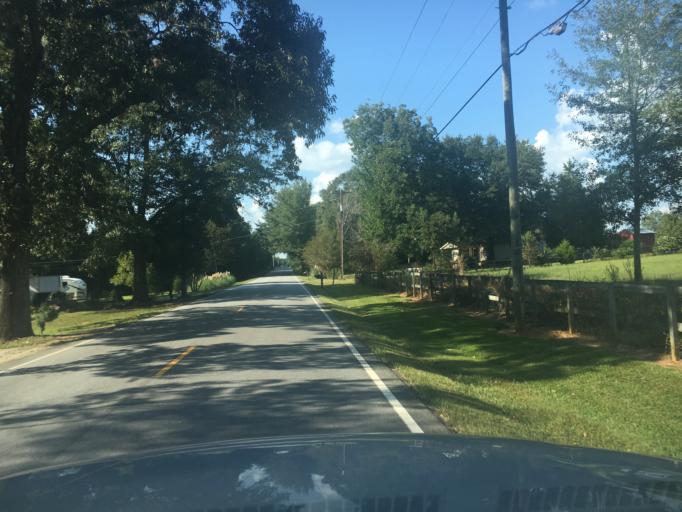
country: US
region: South Carolina
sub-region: Greenville County
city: Fountain Inn
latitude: 34.5970
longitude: -82.2274
